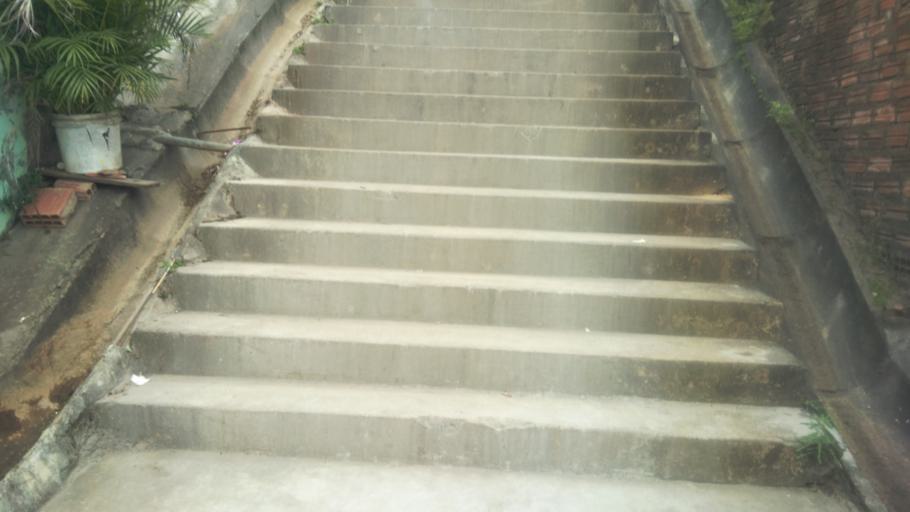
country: BR
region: Pernambuco
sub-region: Vicencia
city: Vicencia
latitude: -7.6612
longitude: -35.3212
